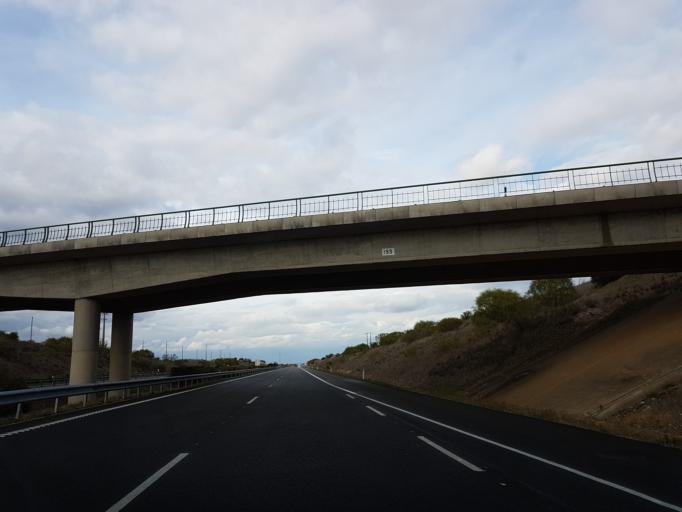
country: PT
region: Beja
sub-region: Aljustrel
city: Aljustrel
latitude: 37.8971
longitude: -8.2404
